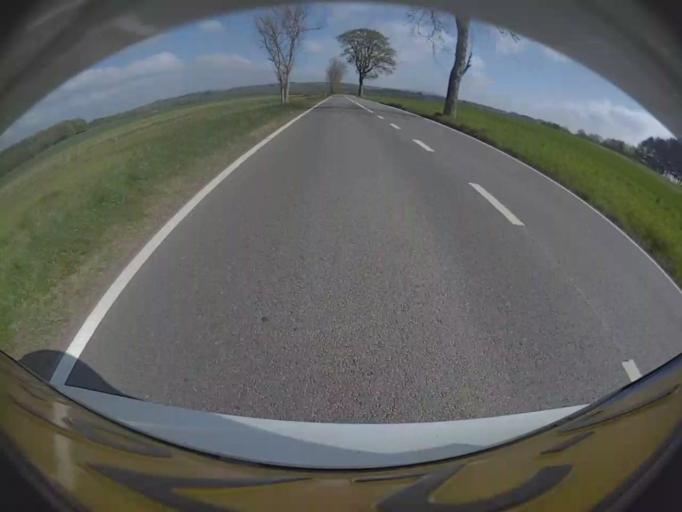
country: BE
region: Wallonia
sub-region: Province du Luxembourg
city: Tellin
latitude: 50.1048
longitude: 5.2333
